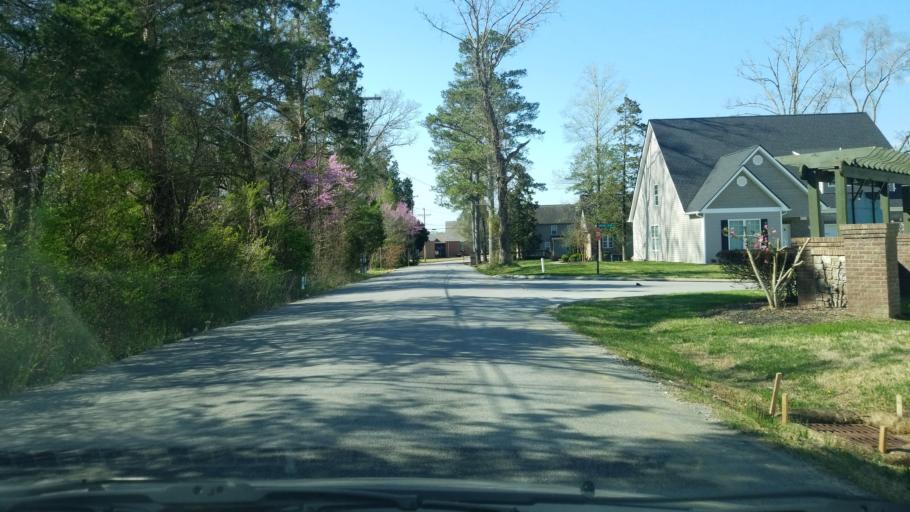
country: US
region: Tennessee
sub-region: Hamilton County
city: Harrison
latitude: 35.0602
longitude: -85.1459
